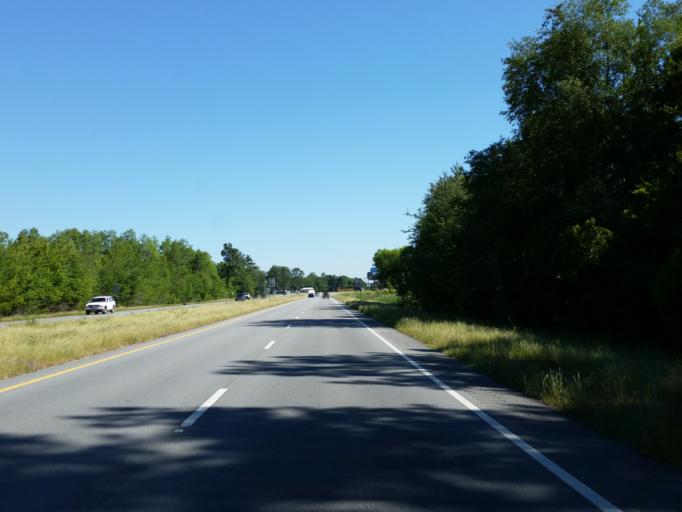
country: US
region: Georgia
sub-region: Lowndes County
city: Valdosta
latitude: 30.7059
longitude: -83.2123
